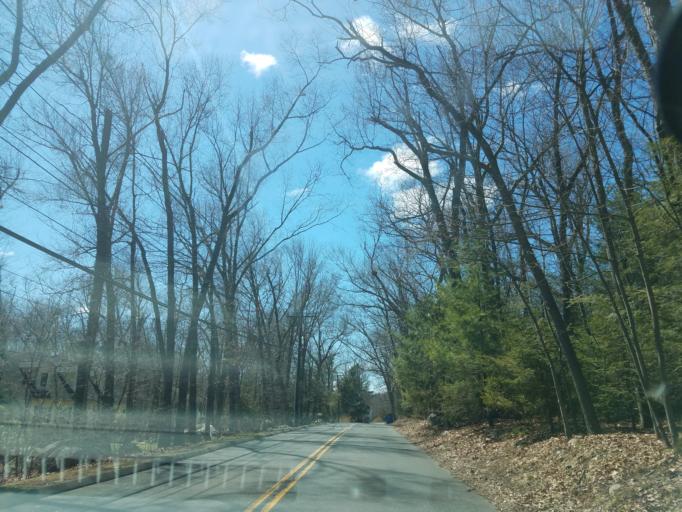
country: US
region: Connecticut
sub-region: Hartford County
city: Collinsville
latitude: 41.7824
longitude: -72.9007
